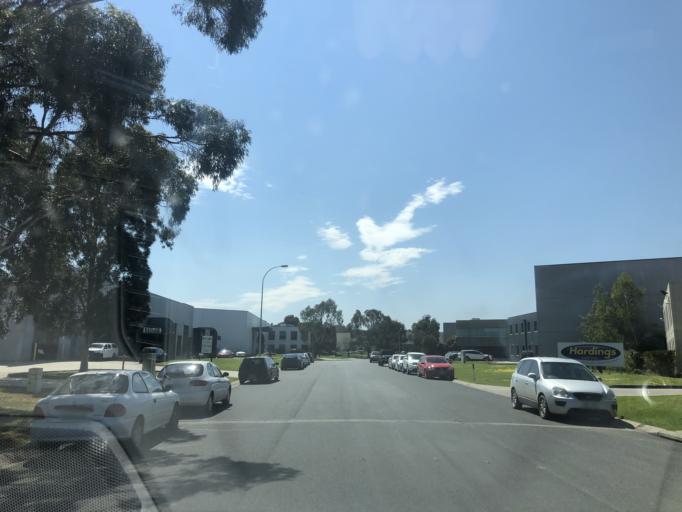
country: AU
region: Victoria
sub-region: Casey
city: Hampton Park
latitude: -38.0266
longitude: 145.2307
